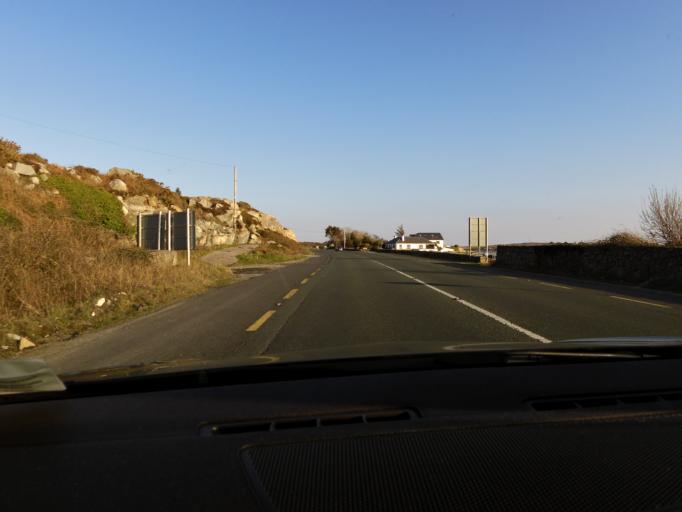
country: IE
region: Connaught
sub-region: County Galway
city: Oughterard
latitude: 53.2872
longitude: -9.5474
